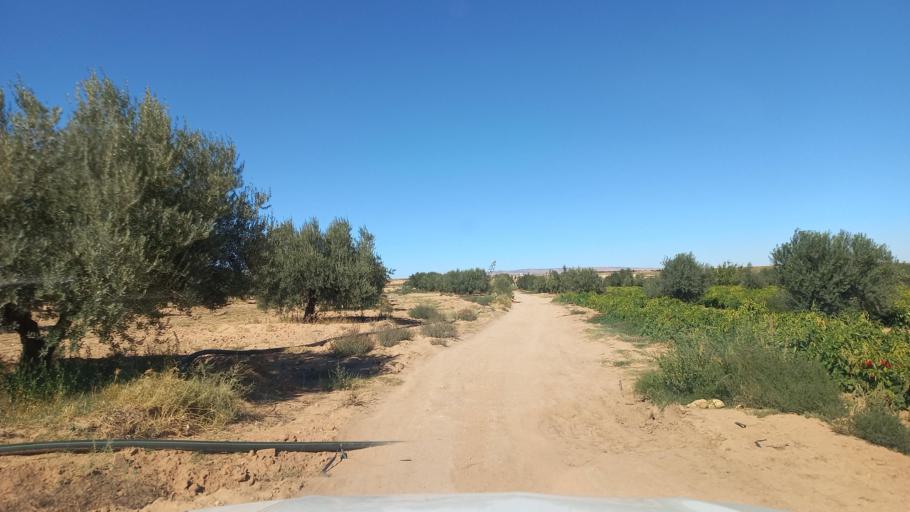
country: TN
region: Al Qasrayn
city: Sbiba
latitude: 35.4034
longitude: 9.0878
